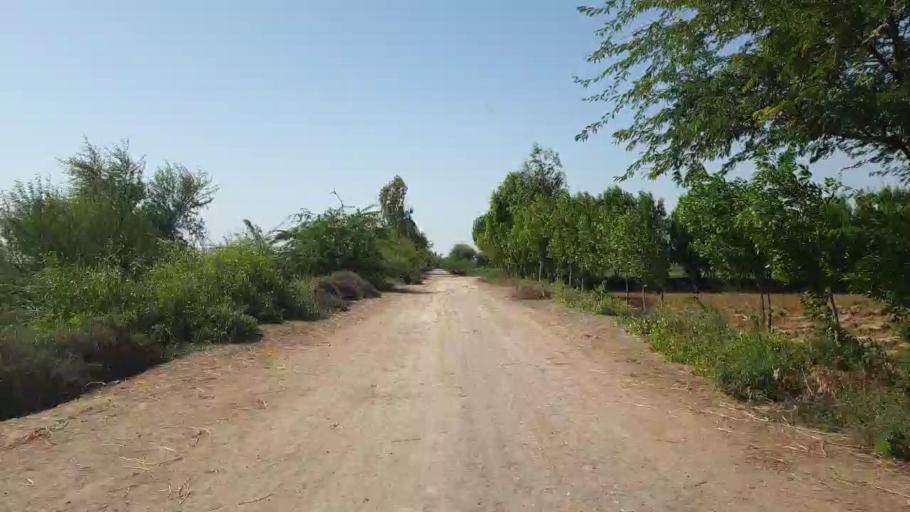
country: PK
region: Sindh
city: Tando Bago
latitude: 24.7048
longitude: 69.0251
